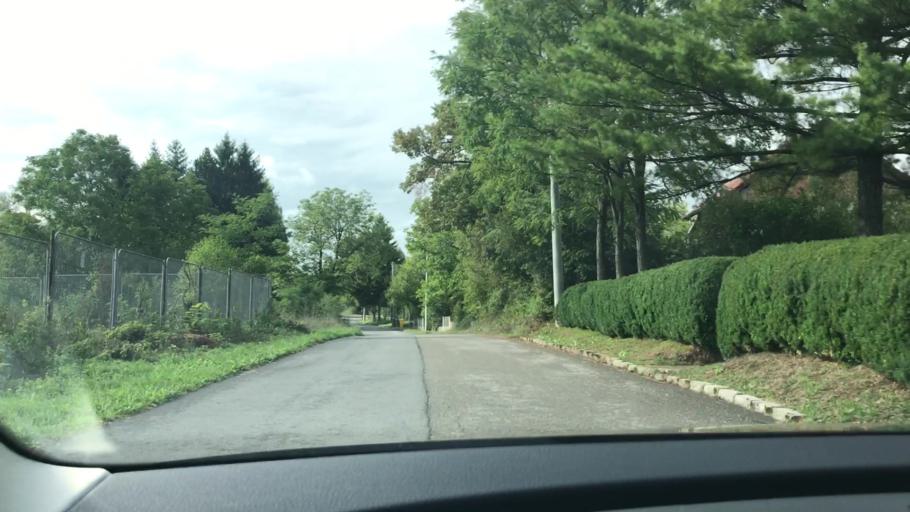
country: BA
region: Federation of Bosnia and Herzegovina
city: Izacic
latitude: 44.8772
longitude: 15.7145
